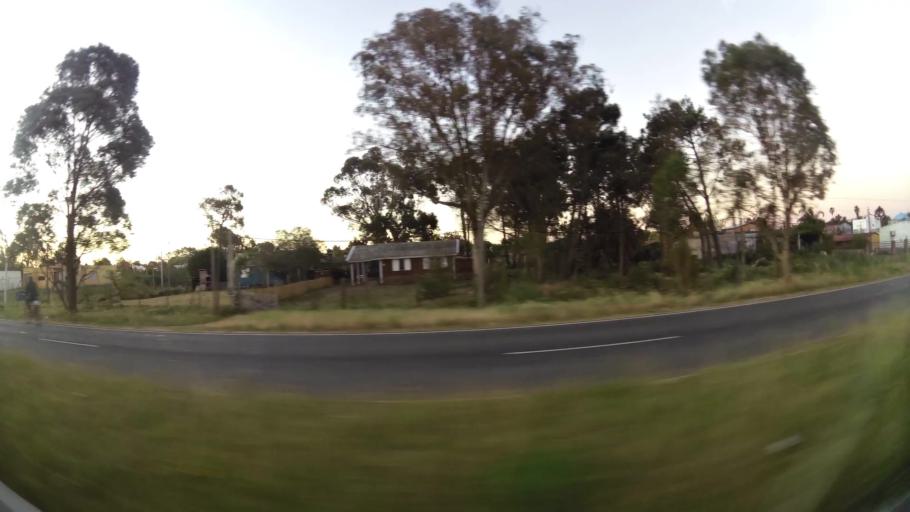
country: UY
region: Canelones
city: Barra de Carrasco
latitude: -34.8285
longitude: -55.9424
